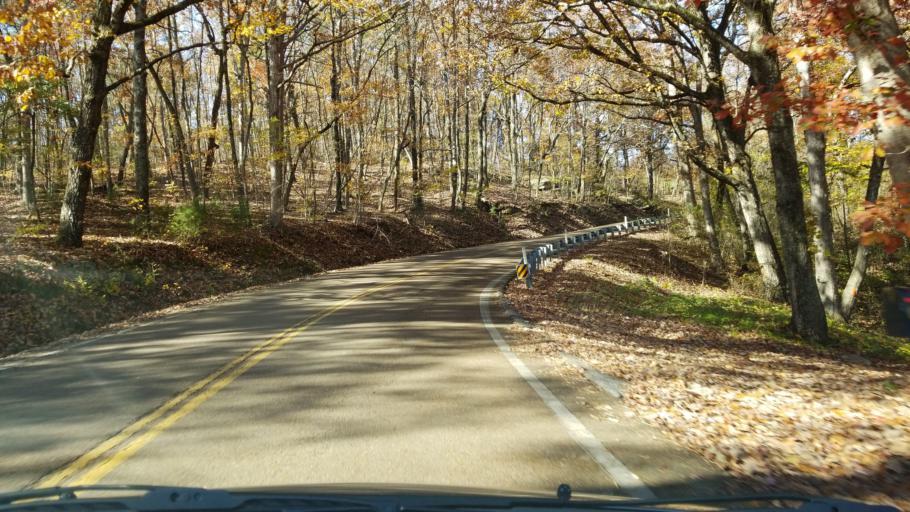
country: US
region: Tennessee
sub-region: Hamilton County
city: Soddy-Daisy
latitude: 35.2539
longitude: -85.2015
